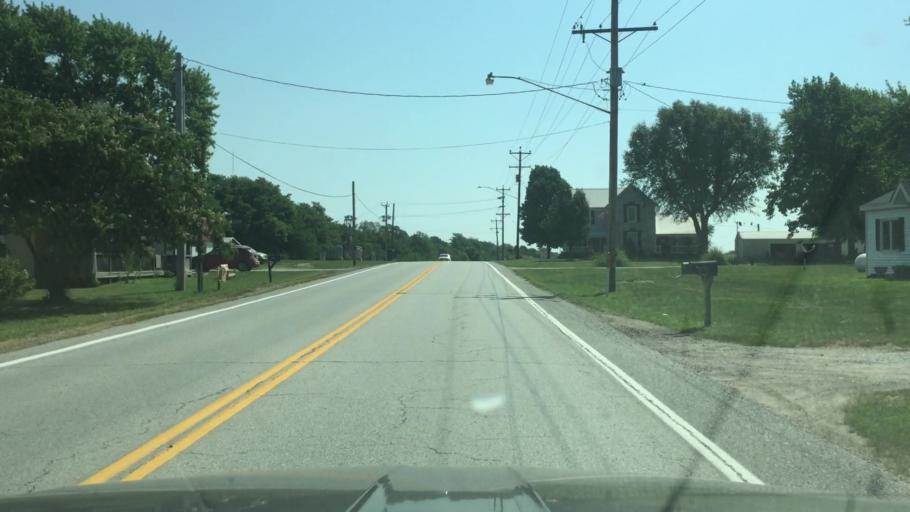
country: US
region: Missouri
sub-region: Moniteau County
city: Tipton
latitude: 38.6703
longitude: -92.8711
